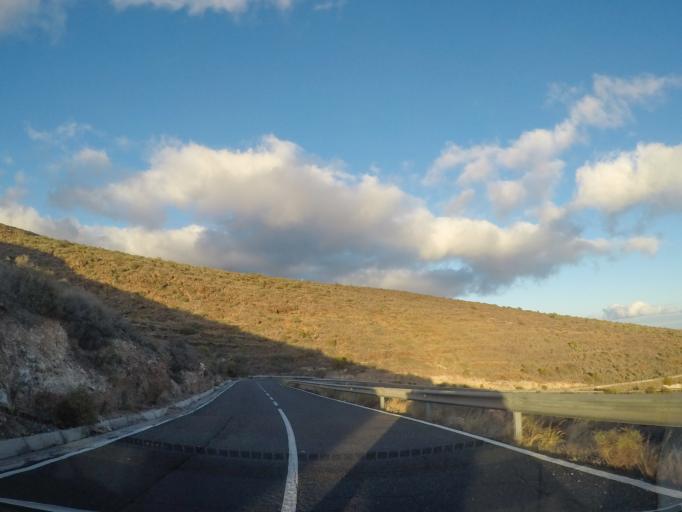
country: ES
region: Canary Islands
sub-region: Provincia de Santa Cruz de Tenerife
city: Alajero
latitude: 28.0395
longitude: -17.2275
